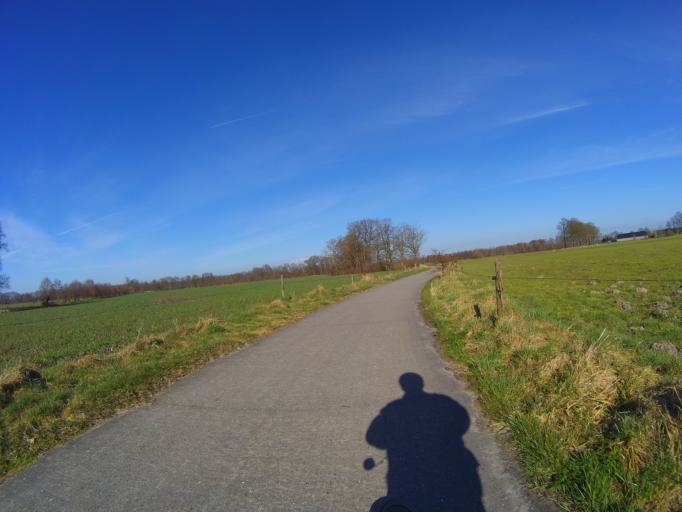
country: NL
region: Utrecht
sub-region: Gemeente Utrechtse Heuvelrug
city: Overberg
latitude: 52.0616
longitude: 5.4915
